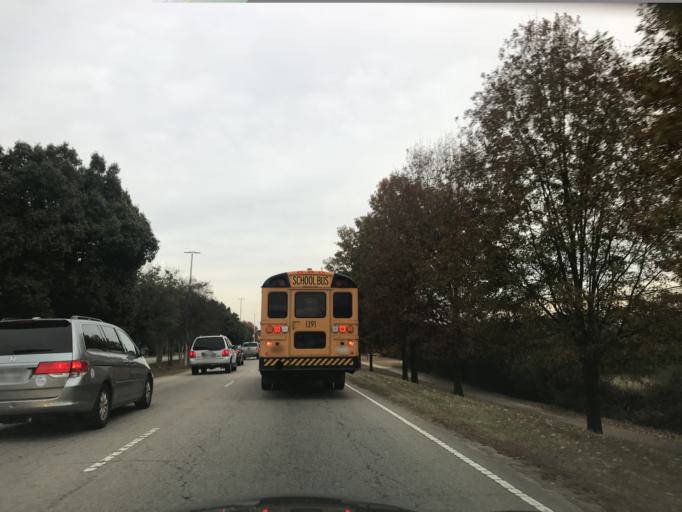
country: US
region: North Carolina
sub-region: Wake County
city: West Raleigh
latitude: 35.7831
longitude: -78.6812
